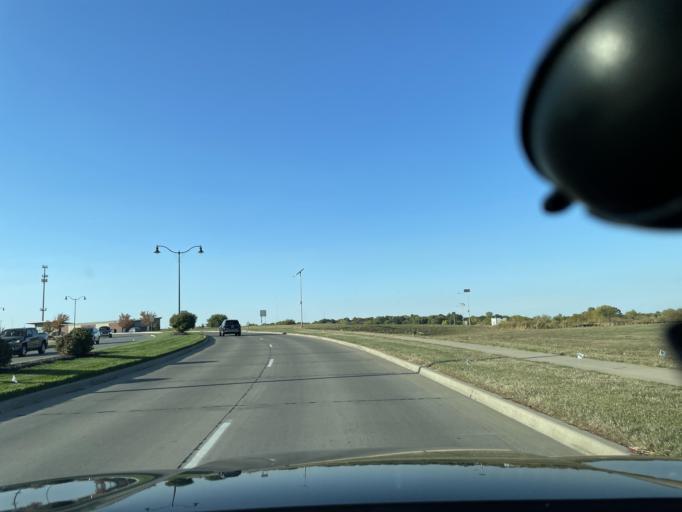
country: US
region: Missouri
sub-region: Andrew County
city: Country Club Village
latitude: 39.8148
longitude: -94.8074
